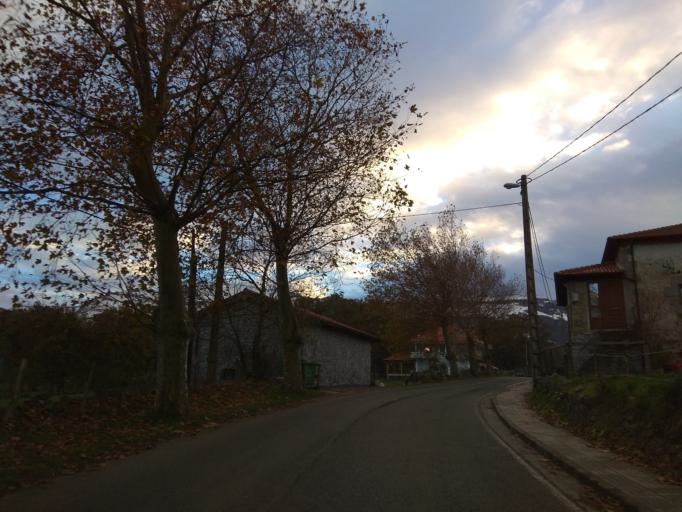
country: ES
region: Cantabria
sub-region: Provincia de Cantabria
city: Arredondo
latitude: 43.1924
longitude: -3.5689
